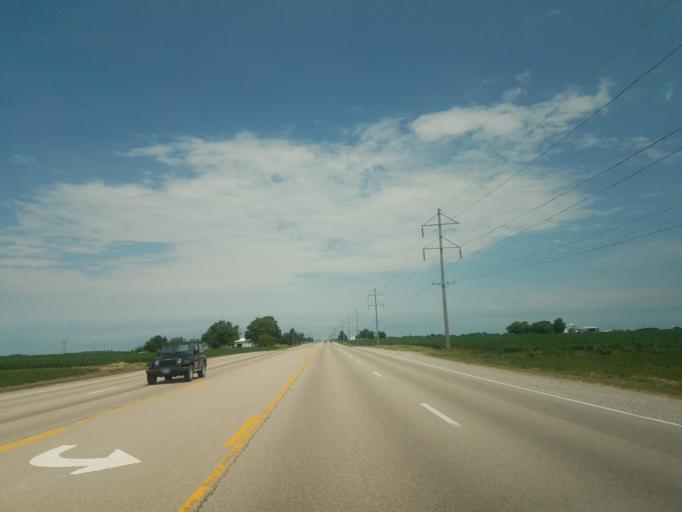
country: US
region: Illinois
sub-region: McLean County
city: Downs
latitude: 40.4359
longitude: -88.9016
